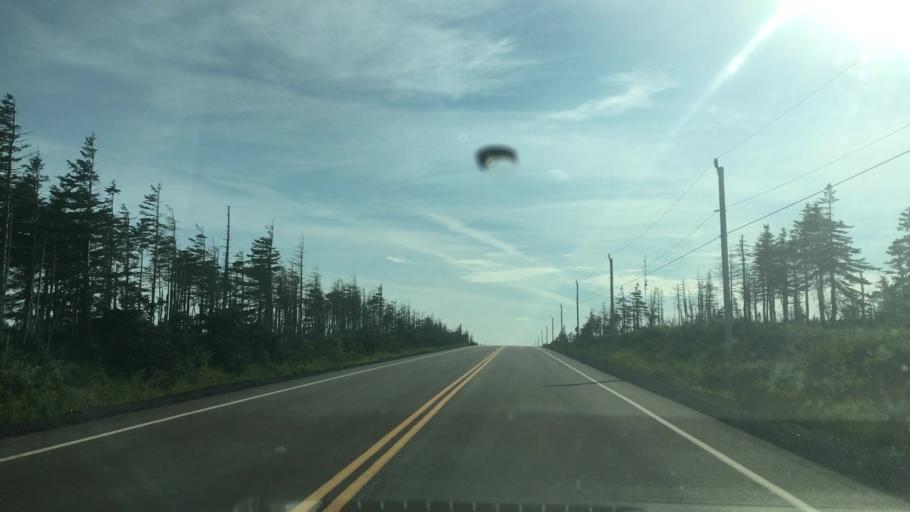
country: CA
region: Nova Scotia
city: Sydney Mines
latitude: 46.8216
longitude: -60.6644
